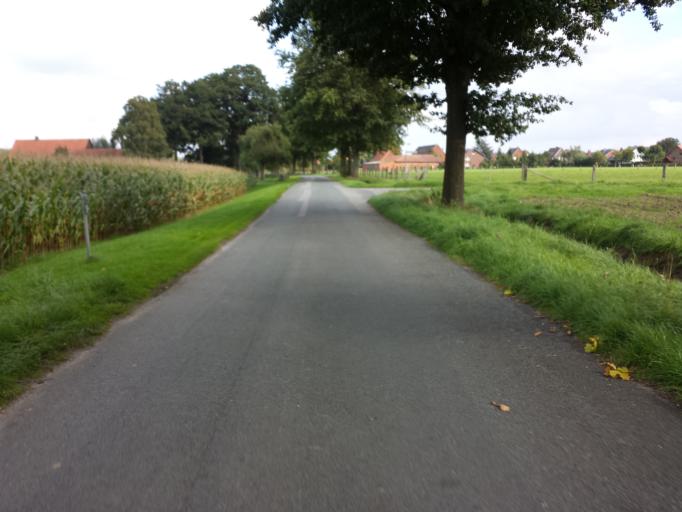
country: DE
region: North Rhine-Westphalia
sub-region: Regierungsbezirk Detmold
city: Langenberg
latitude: 51.7860
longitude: 8.3056
